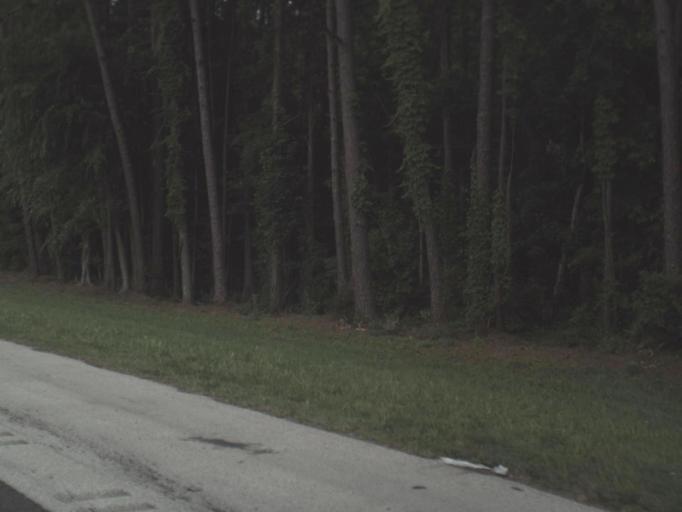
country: US
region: Florida
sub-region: Saint Johns County
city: Saint Augustine
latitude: 29.8962
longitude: -81.4054
